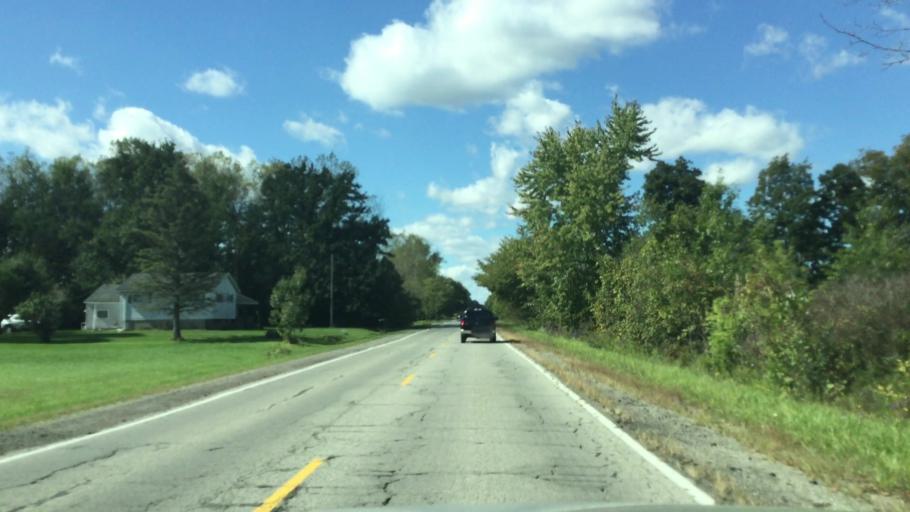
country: US
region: Michigan
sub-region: Genesee County
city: Swartz Creek
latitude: 42.9425
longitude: -83.8170
